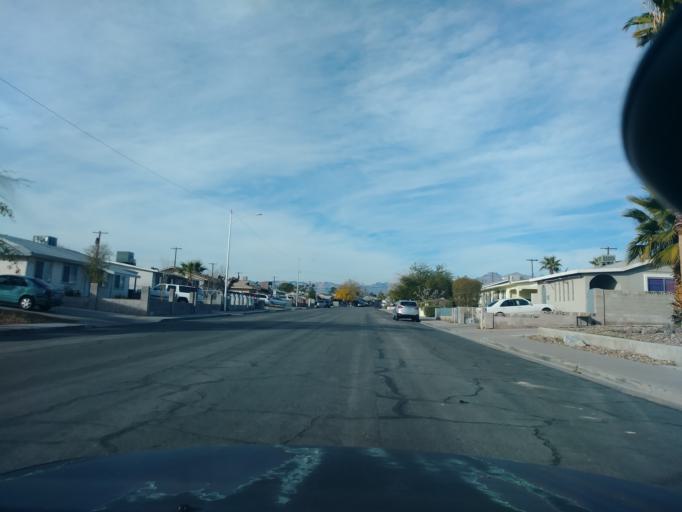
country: US
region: Nevada
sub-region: Clark County
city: Spring Valley
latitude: 36.1623
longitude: -115.2349
